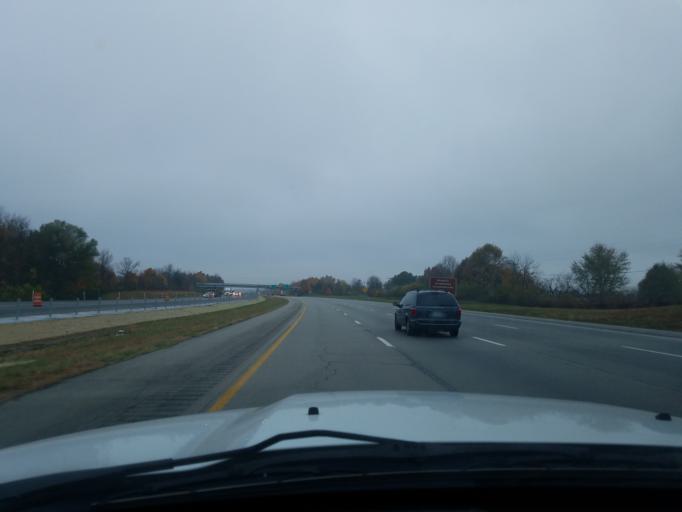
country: US
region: Kentucky
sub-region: Hardin County
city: Elizabethtown
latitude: 37.7307
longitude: -85.8164
